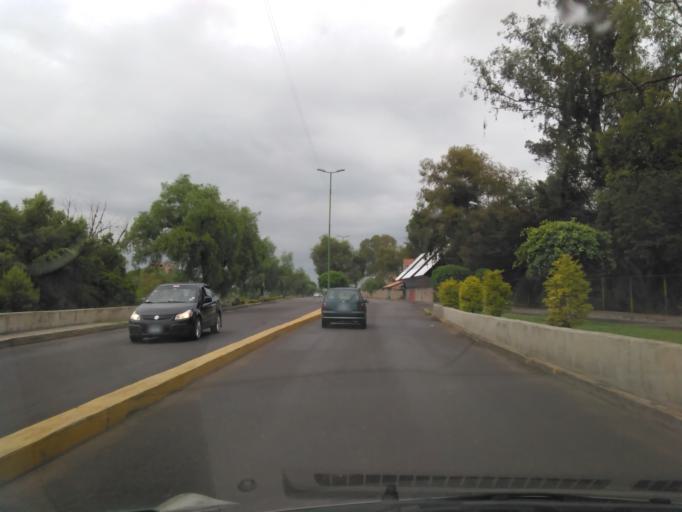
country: BO
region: Cochabamba
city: Cochabamba
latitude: -17.3977
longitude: -66.1682
